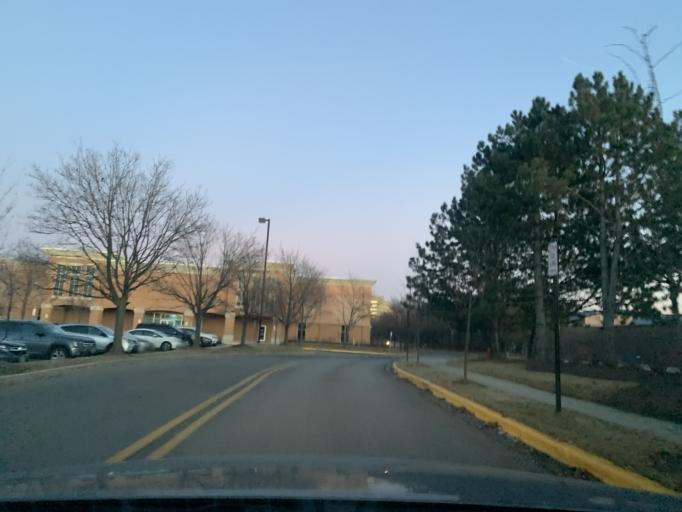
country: US
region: Illinois
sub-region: Cook County
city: Hoffman Estates
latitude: 42.0534
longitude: -88.0433
